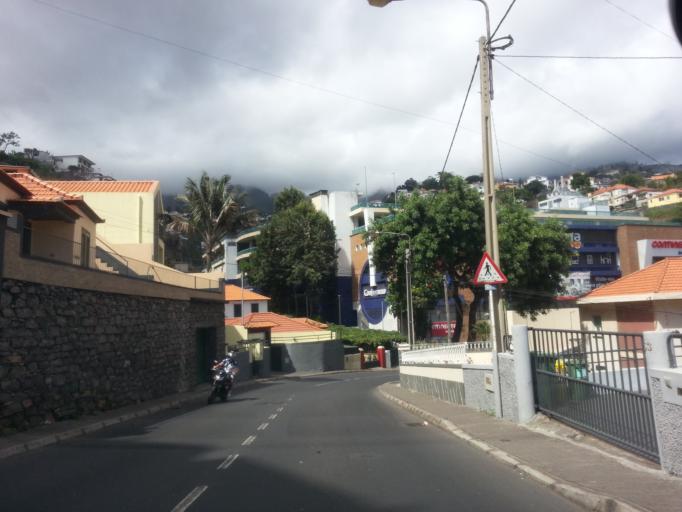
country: PT
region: Madeira
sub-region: Funchal
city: Nossa Senhora do Monte
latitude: 32.6592
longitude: -16.9202
